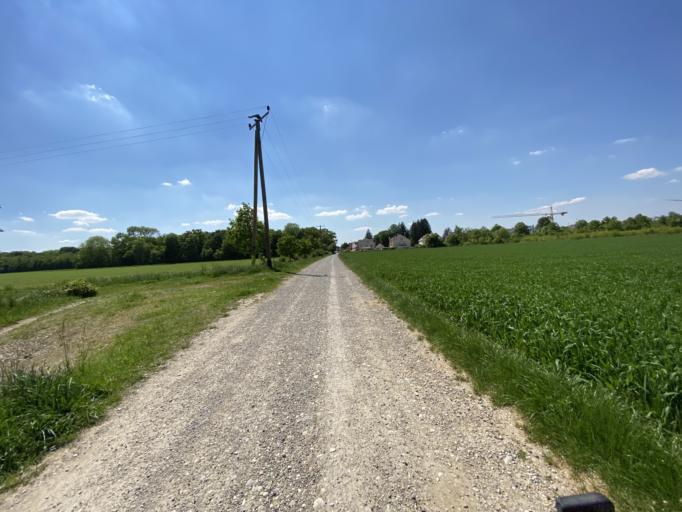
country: DE
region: Bavaria
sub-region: Upper Bavaria
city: Germering
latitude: 48.1317
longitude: 11.3916
